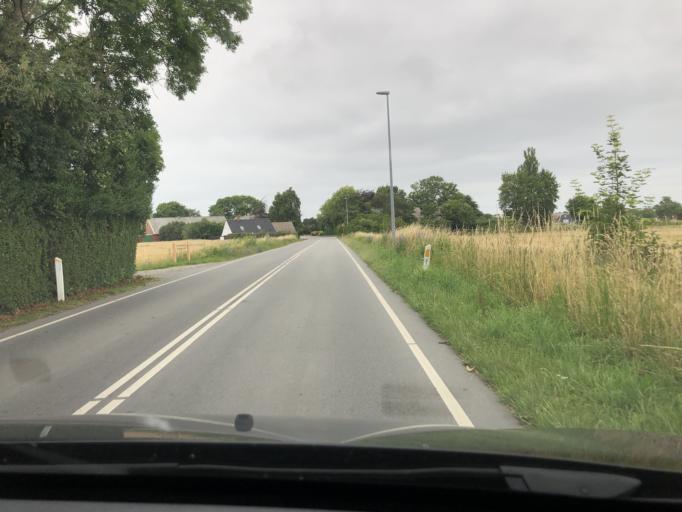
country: DK
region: South Denmark
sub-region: AEro Kommune
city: Marstal
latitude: 54.8477
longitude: 10.4966
